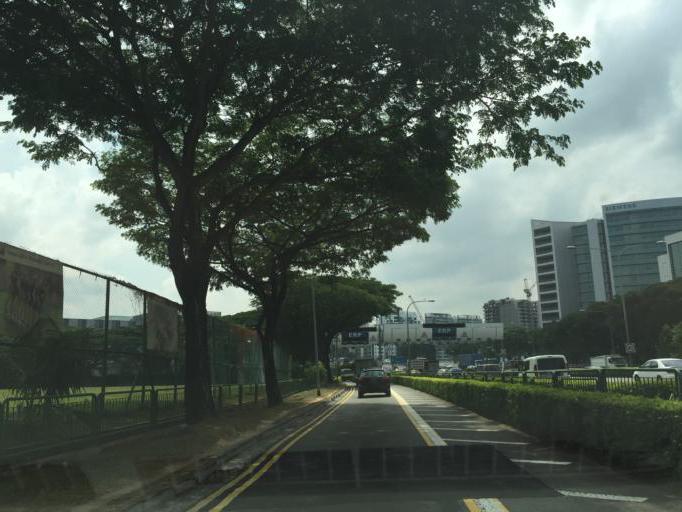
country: SG
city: Singapore
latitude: 1.3254
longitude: 103.8711
